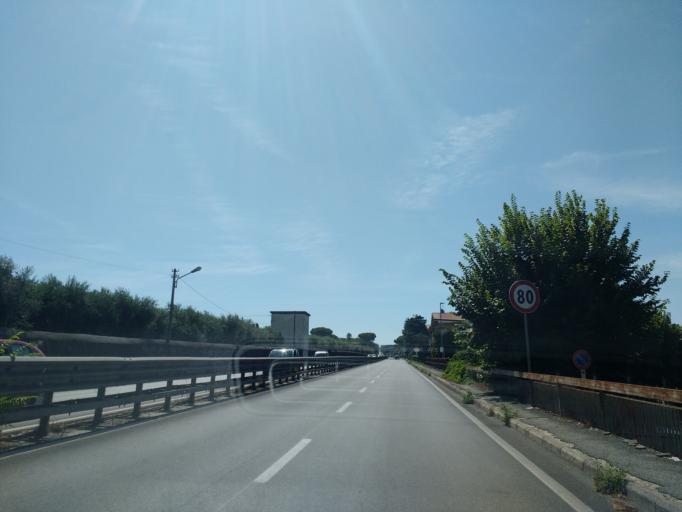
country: IT
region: Latium
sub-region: Citta metropolitana di Roma Capitale
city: Marino
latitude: 41.7650
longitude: 12.6183
